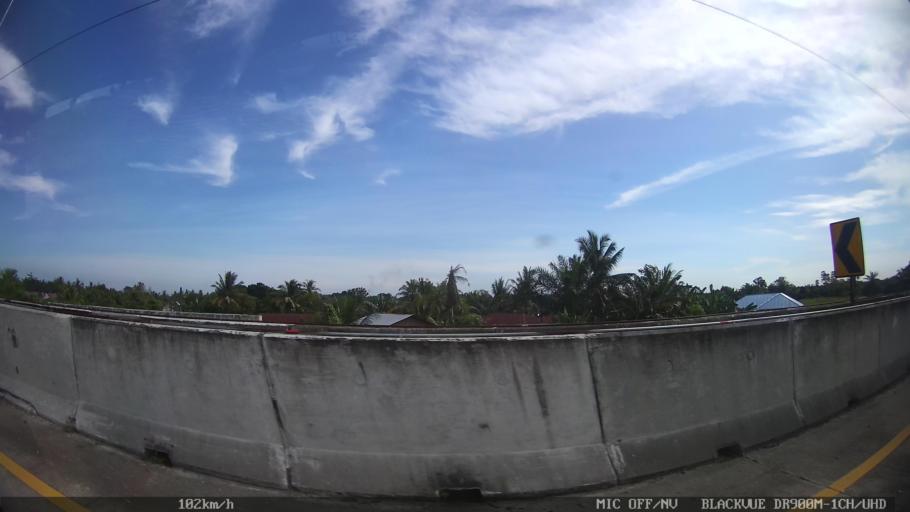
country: ID
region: North Sumatra
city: Sunggal
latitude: 3.6379
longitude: 98.5783
